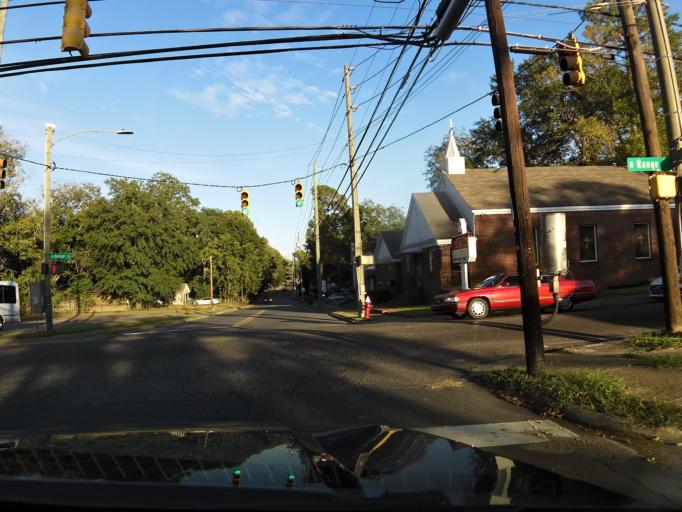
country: US
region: Alabama
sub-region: Houston County
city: Dothan
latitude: 31.2277
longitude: -85.3831
